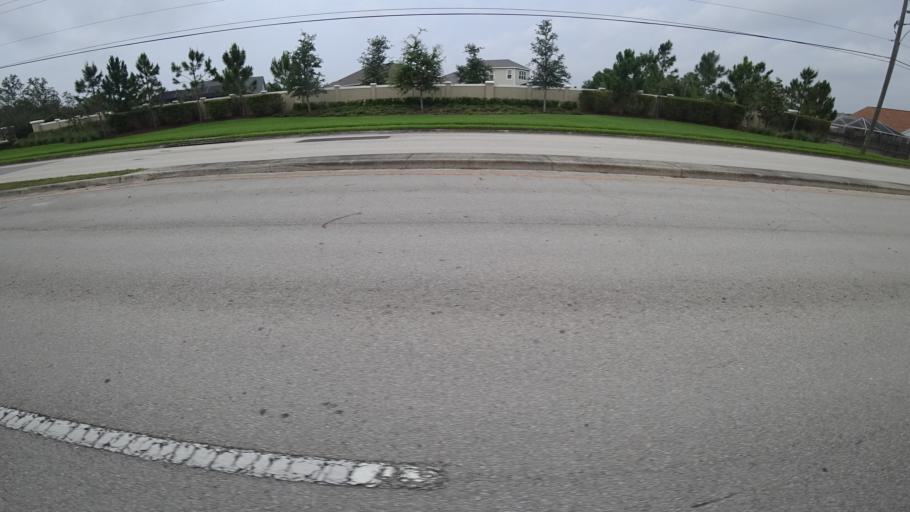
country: US
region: Florida
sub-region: Sarasota County
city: North Sarasota
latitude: 27.4149
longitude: -82.5052
